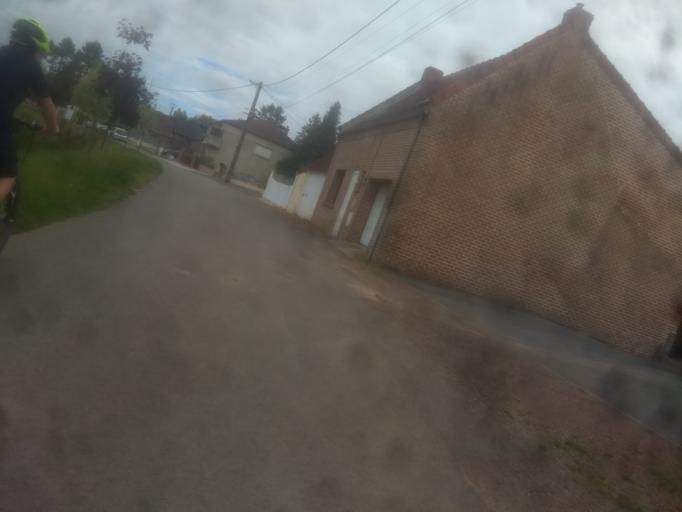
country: FR
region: Nord-Pas-de-Calais
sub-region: Departement du Pas-de-Calais
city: Maroeuil
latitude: 50.3204
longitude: 2.7068
